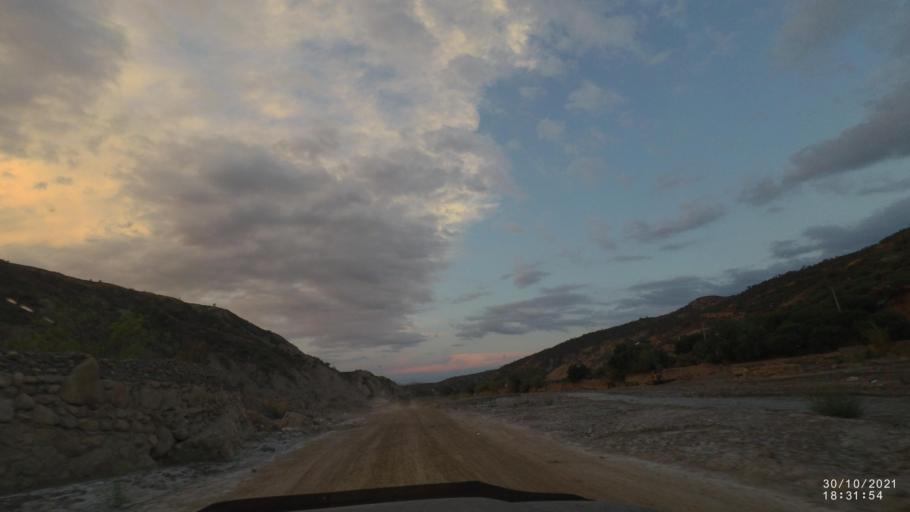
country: BO
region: Cochabamba
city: Sipe Sipe
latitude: -17.5633
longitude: -66.3776
